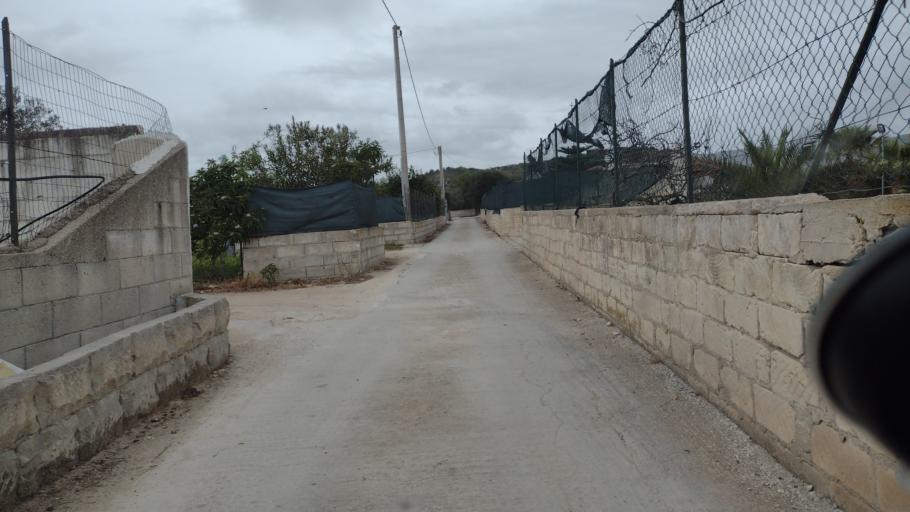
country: IT
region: Sicily
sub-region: Provincia di Siracusa
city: Avola
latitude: 36.8977
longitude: 15.1109
